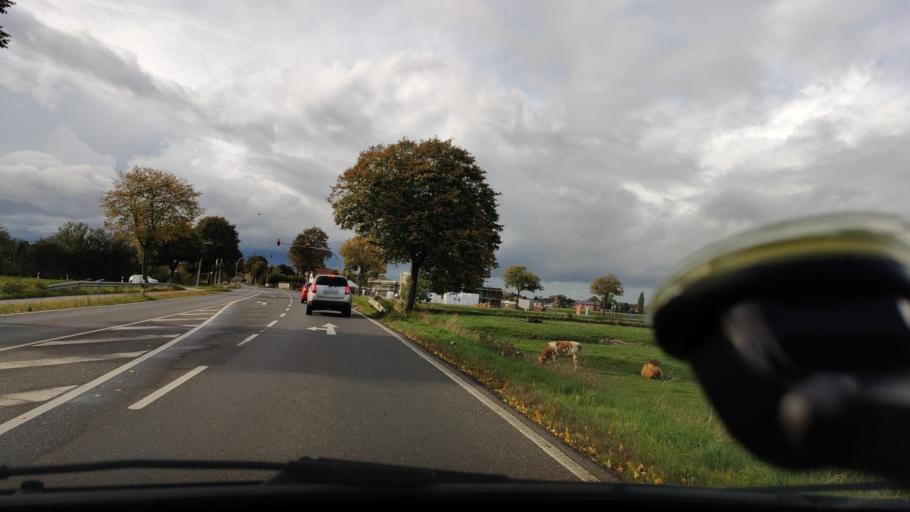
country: DE
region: North Rhine-Westphalia
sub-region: Regierungsbezirk Koln
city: Heinsberg
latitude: 51.0936
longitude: 6.0914
